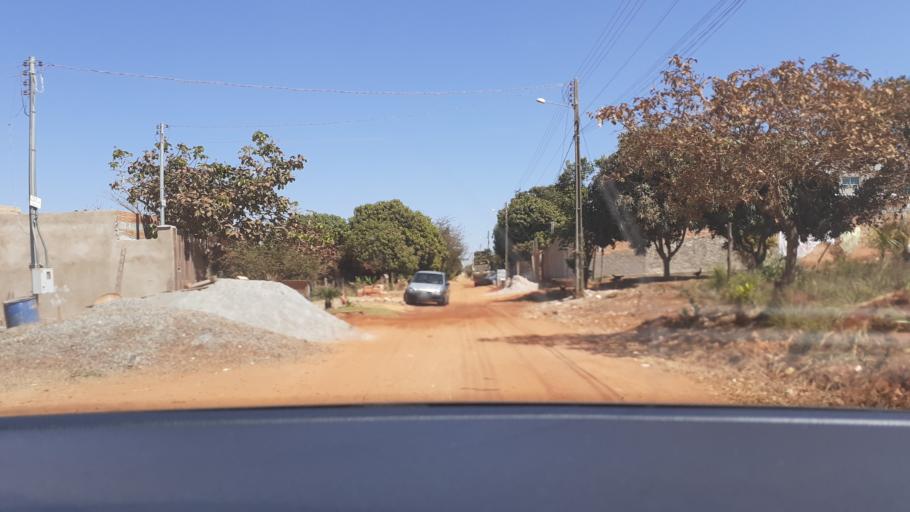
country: BR
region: Goias
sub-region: Aparecida De Goiania
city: Aparecida de Goiania
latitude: -16.8720
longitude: -49.2786
